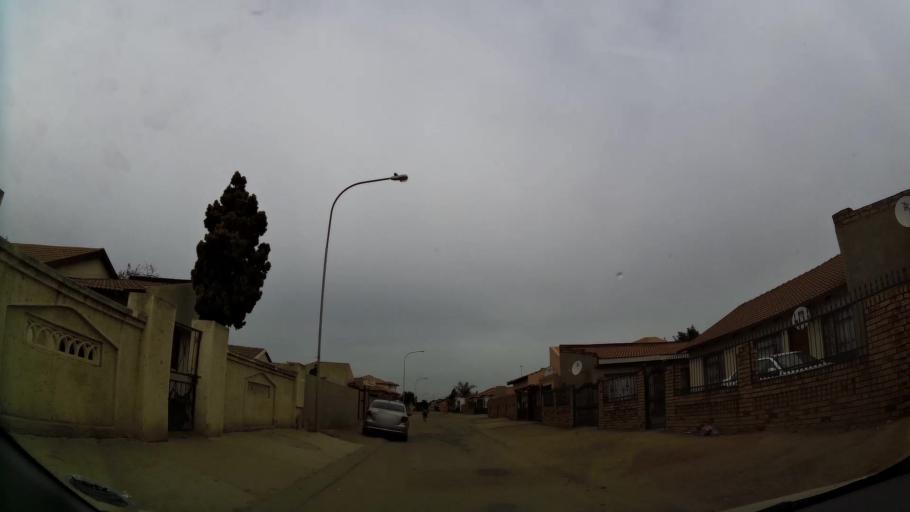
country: ZA
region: Gauteng
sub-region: City of Tshwane Metropolitan Municipality
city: Pretoria
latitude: -25.7148
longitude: 28.3432
